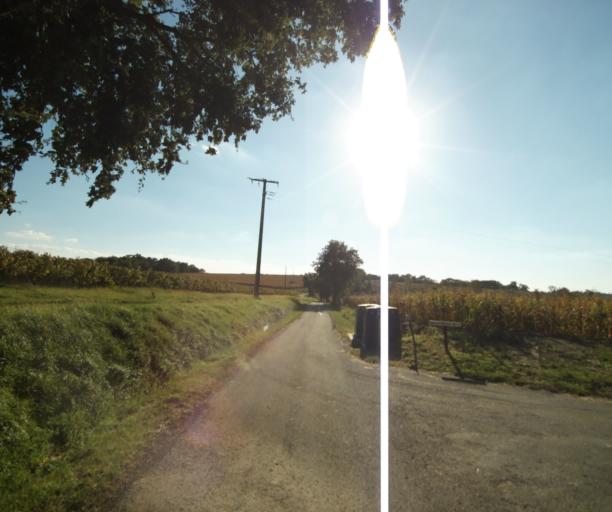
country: FR
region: Midi-Pyrenees
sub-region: Departement du Gers
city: Eauze
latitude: 43.7967
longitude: 0.1256
